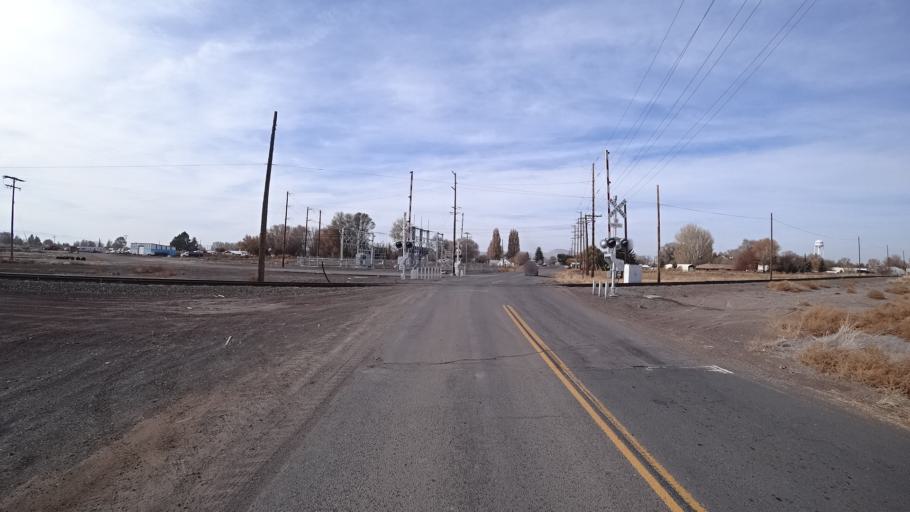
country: US
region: California
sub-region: Siskiyou County
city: Tulelake
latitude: 41.9537
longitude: -121.4703
